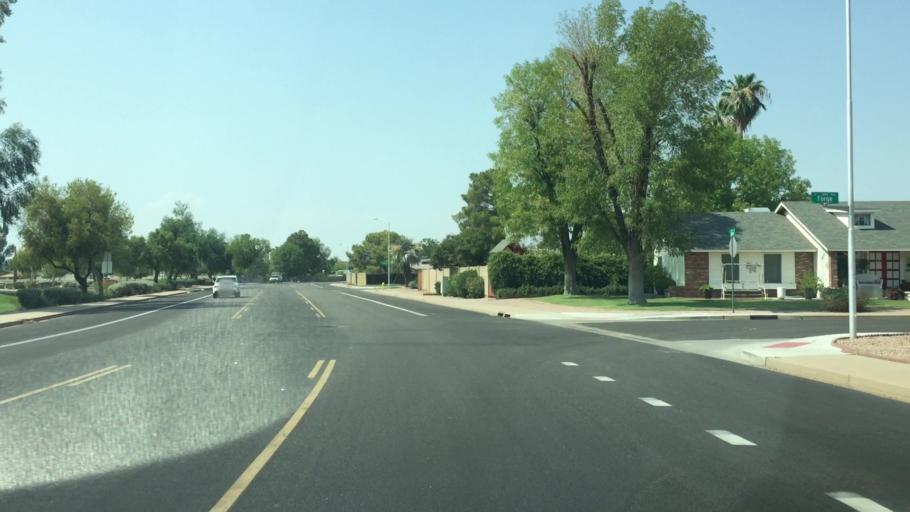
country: US
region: Arizona
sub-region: Maricopa County
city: Gilbert
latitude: 33.3954
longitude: -111.7614
